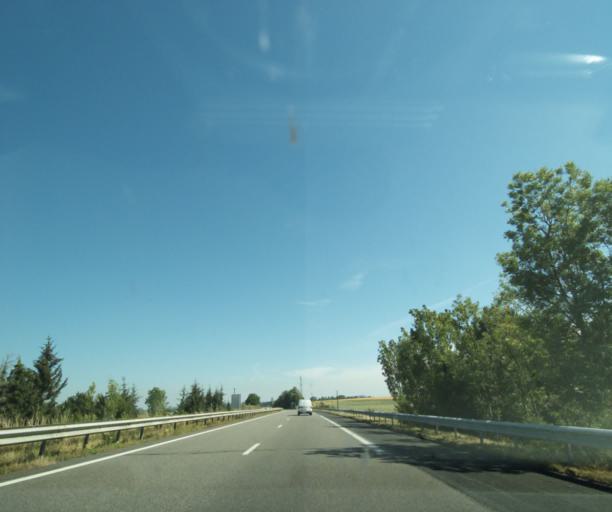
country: FR
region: Lorraine
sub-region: Departement des Vosges
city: Bulgneville
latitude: 48.2518
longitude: 5.8646
